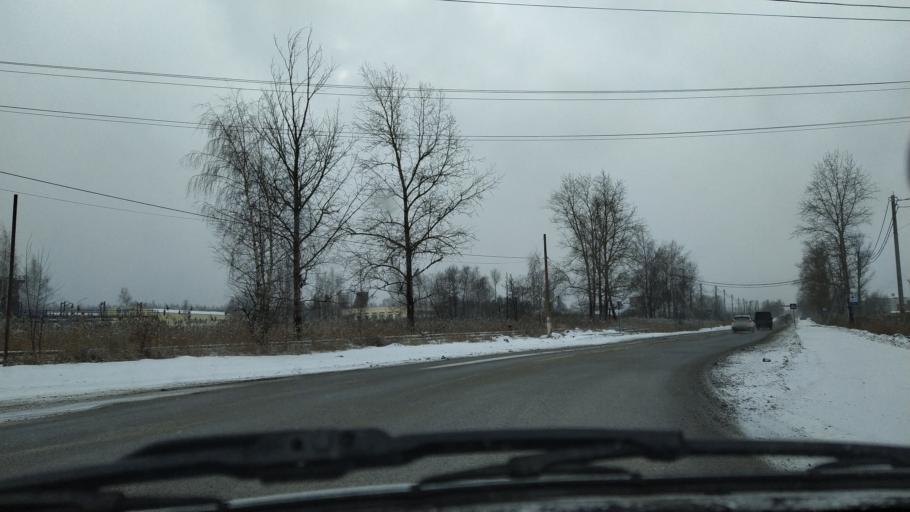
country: RU
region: Moskovskaya
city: Lopatinskiy
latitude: 55.3514
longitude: 38.7409
